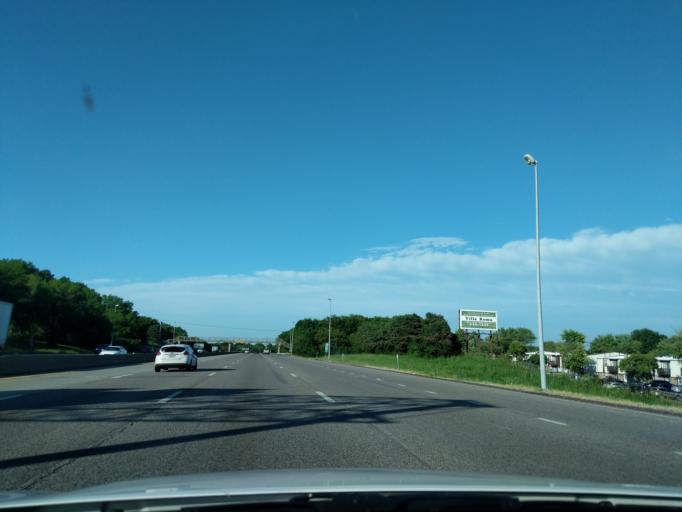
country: US
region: Missouri
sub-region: Saint Louis County
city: Saint George
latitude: 38.5342
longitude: -90.3102
